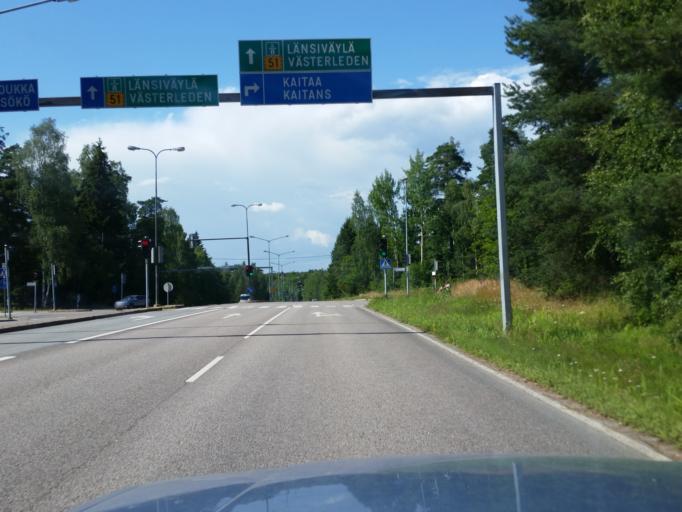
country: FI
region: Uusimaa
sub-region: Helsinki
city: Espoo
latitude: 60.1434
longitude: 24.6759
